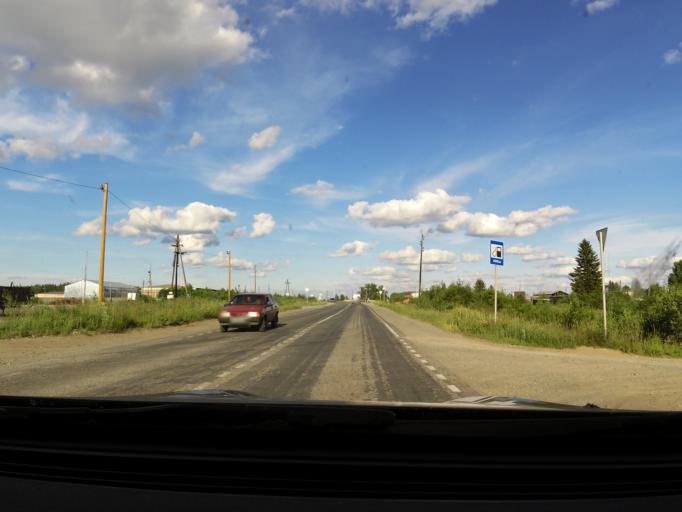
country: RU
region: Kirov
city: Omutninsk
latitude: 58.6892
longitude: 52.1817
